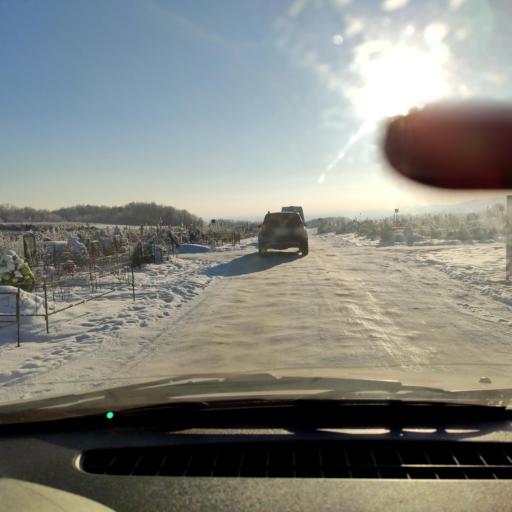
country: RU
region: Bashkortostan
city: Ufa
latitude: 54.8554
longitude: 56.1656
